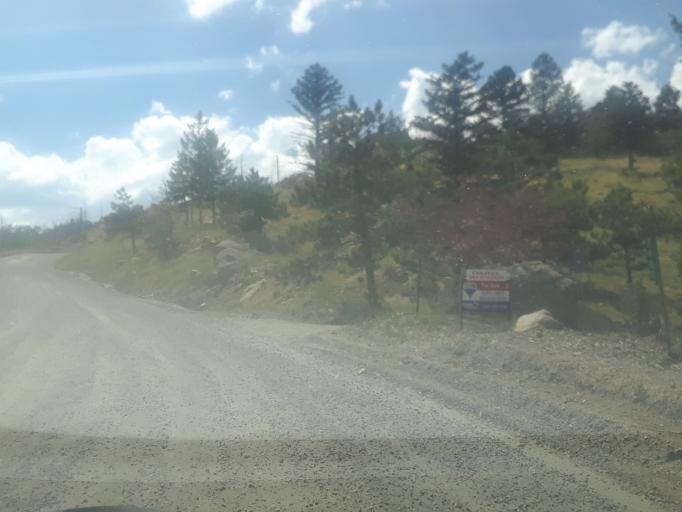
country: US
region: Colorado
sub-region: Boulder County
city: Boulder
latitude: 40.0672
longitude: -105.3773
